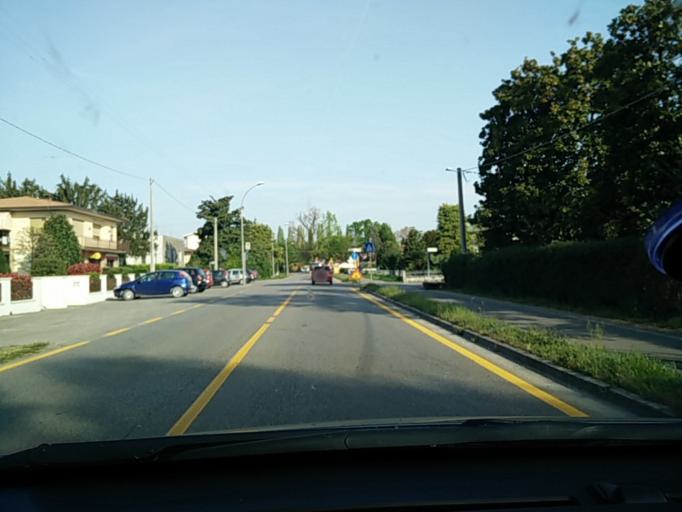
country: IT
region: Veneto
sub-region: Provincia di Treviso
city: Piavon
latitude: 45.7629
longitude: 12.5262
